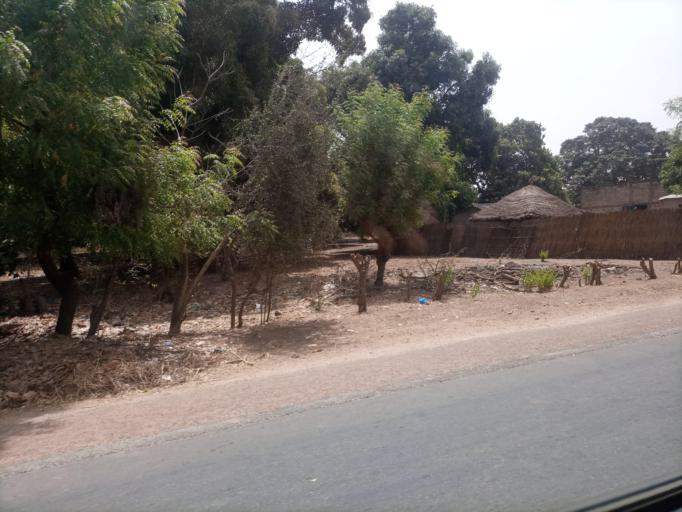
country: SN
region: Fatick
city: Sokone
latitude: 13.7267
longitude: -16.4232
